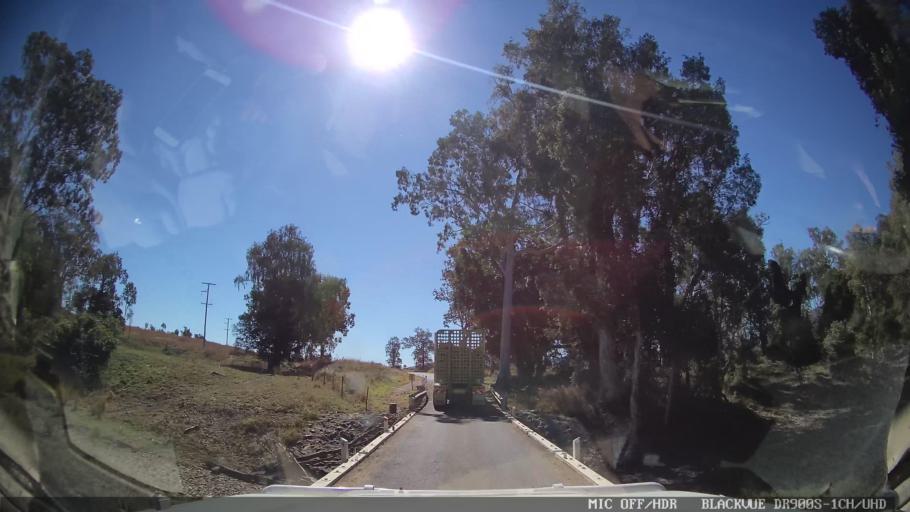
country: AU
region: Queensland
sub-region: Gladstone
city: Toolooa
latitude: -24.2743
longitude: 151.2761
